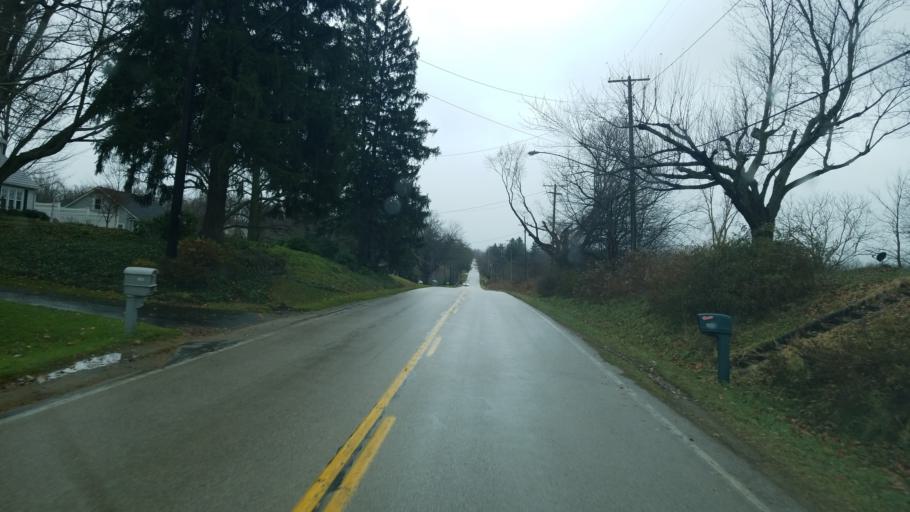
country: US
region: Ohio
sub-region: Ashtabula County
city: Ashtabula
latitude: 41.8376
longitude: -80.8023
